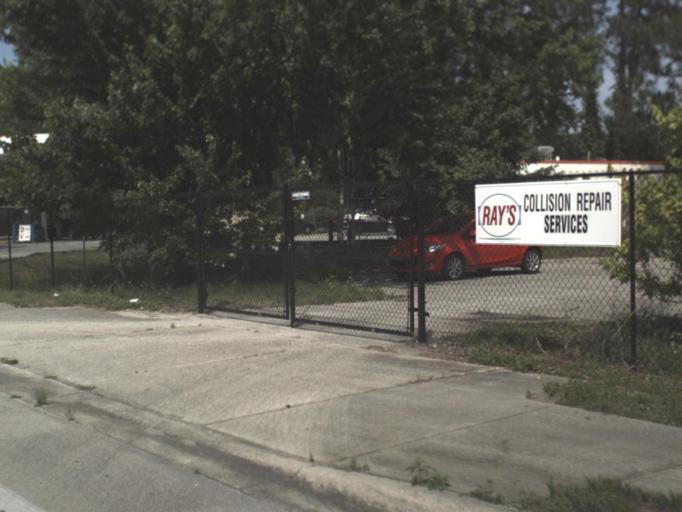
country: US
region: Florida
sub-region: Saint Johns County
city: Saint Augustine South
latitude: 29.8456
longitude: -81.3623
